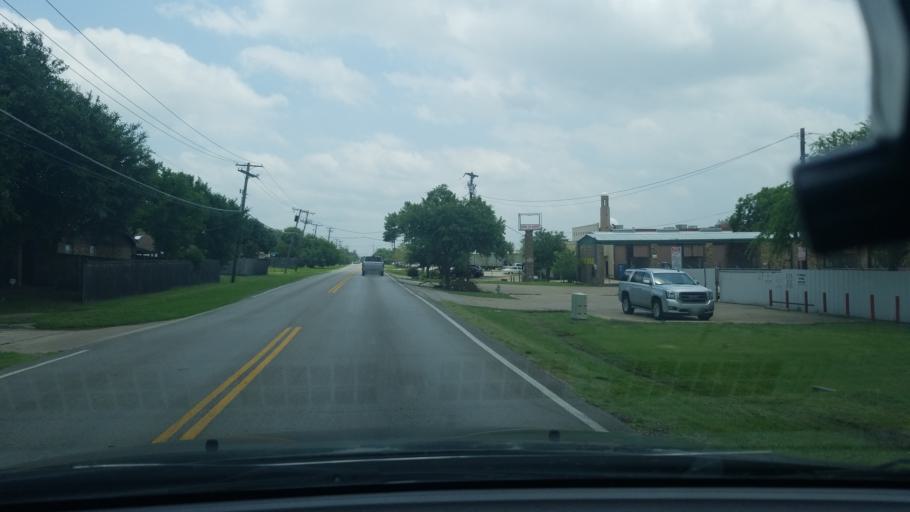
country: US
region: Texas
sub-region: Dallas County
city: Mesquite
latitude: 32.7975
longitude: -96.6186
